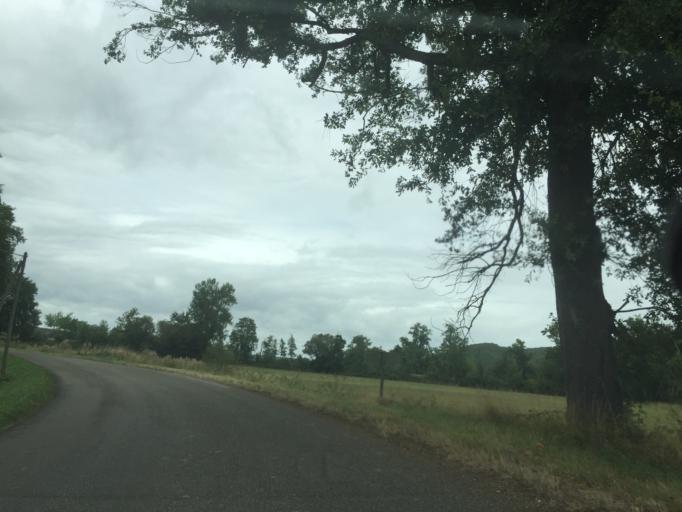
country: FR
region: Midi-Pyrenees
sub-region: Departement du Gers
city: Mielan
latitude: 43.4811
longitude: 0.3257
